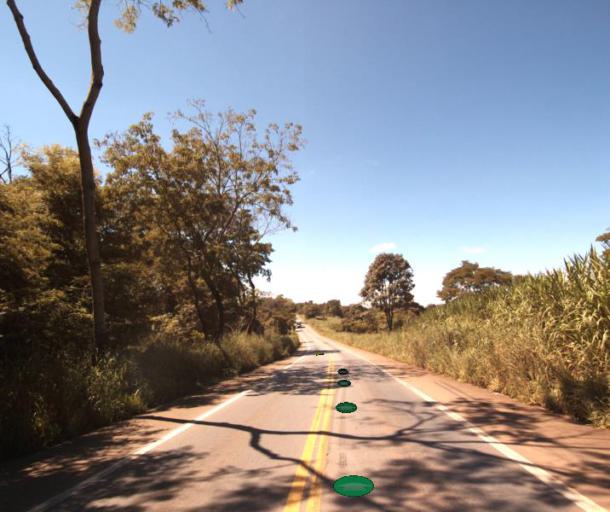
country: BR
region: Goias
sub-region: Jaragua
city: Jaragua
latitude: -15.6103
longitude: -49.4032
